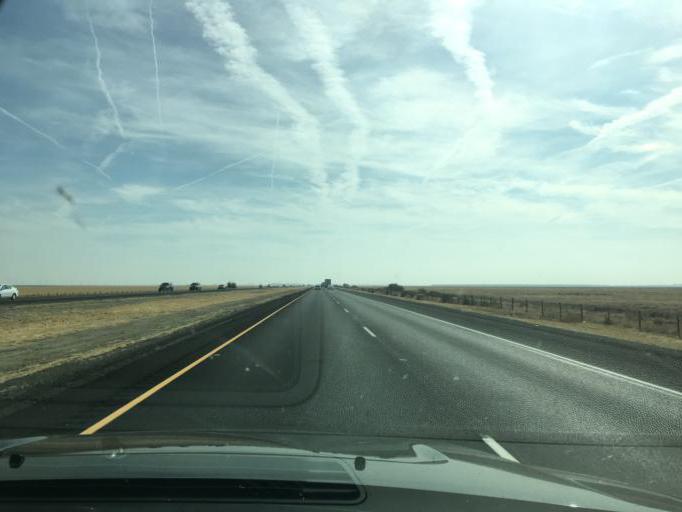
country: US
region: California
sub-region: Kern County
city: Lost Hills
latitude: 35.6589
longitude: -119.6851
